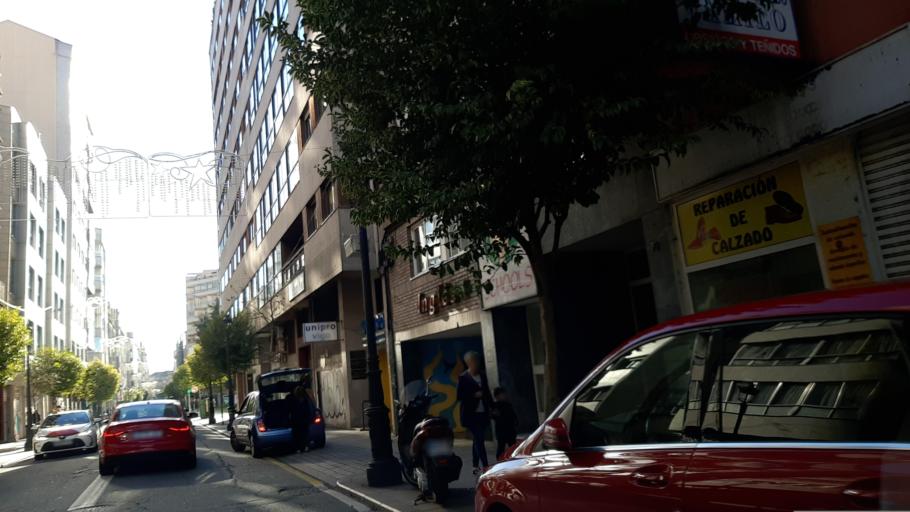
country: ES
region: Galicia
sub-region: Provincia de Pontevedra
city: Vigo
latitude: 42.2319
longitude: -8.7310
